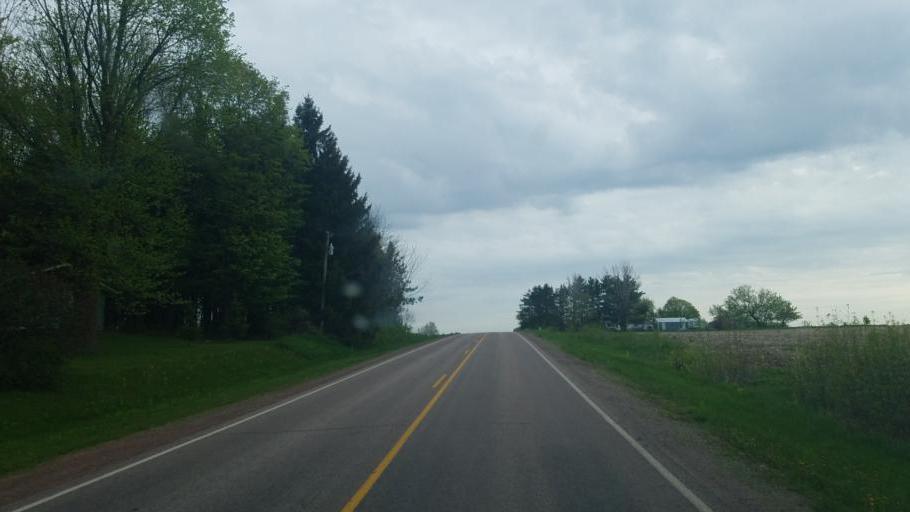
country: US
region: Wisconsin
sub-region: Wood County
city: Marshfield
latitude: 44.5909
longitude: -90.2989
